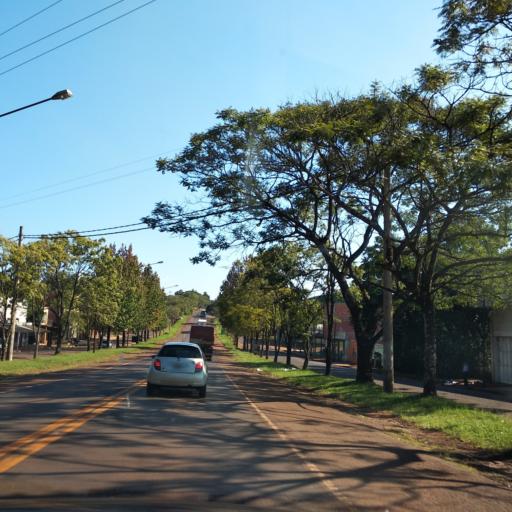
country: AR
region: Misiones
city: Jardin America
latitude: -27.0405
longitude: -55.2315
